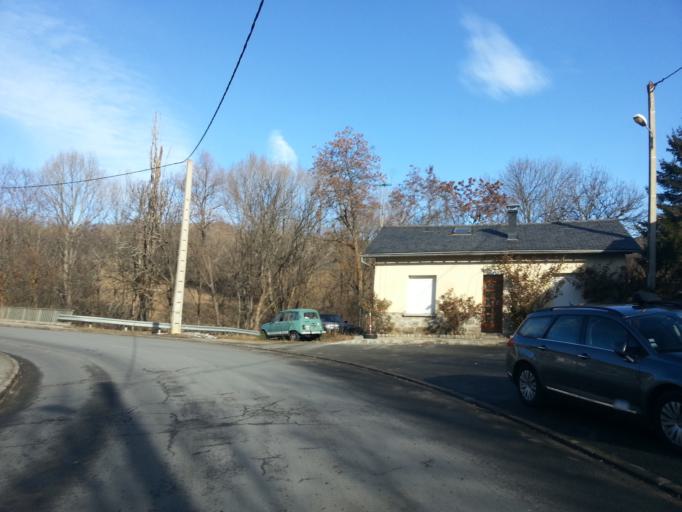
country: ES
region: Catalonia
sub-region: Provincia de Girona
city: Llivia
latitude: 42.4611
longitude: 2.0416
